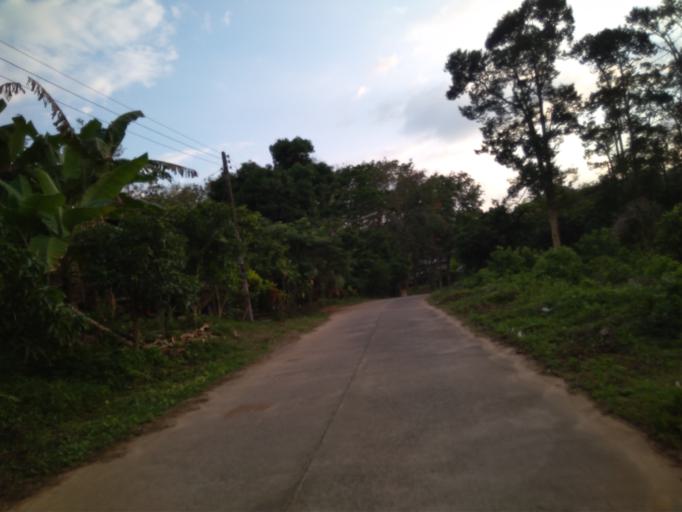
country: TH
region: Phangnga
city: Ko Yao
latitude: 8.1611
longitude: 98.6099
